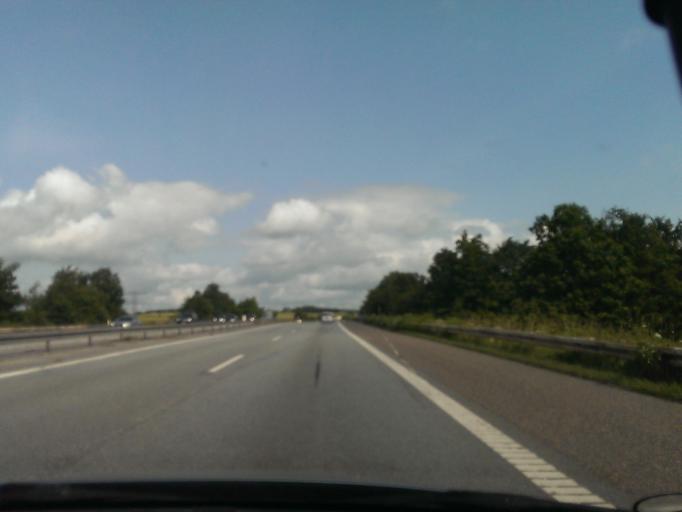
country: DK
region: Central Jutland
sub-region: Randers Kommune
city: Randers
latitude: 56.4737
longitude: 9.9827
